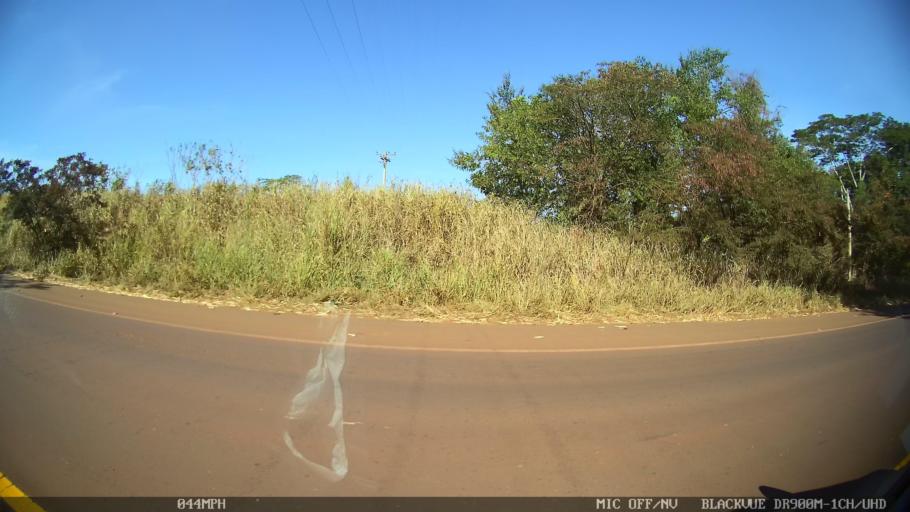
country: BR
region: Sao Paulo
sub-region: Barretos
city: Barretos
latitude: -20.4503
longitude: -48.4540
